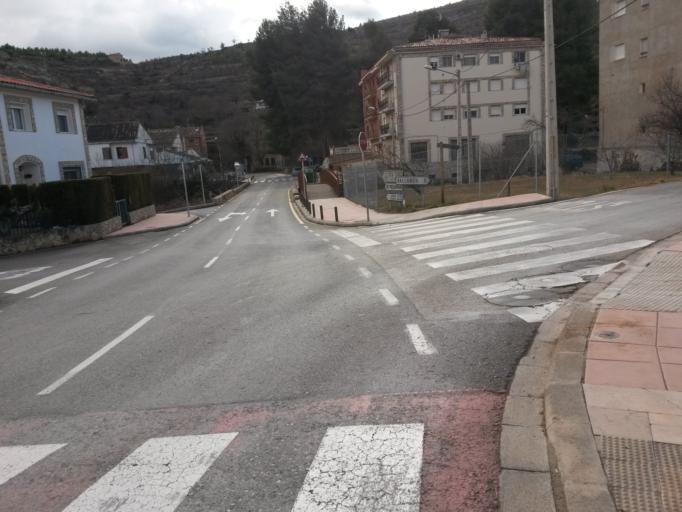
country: ES
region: Valencia
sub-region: Provincia de Valencia
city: Ademuz
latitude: 40.0588
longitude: -1.2866
